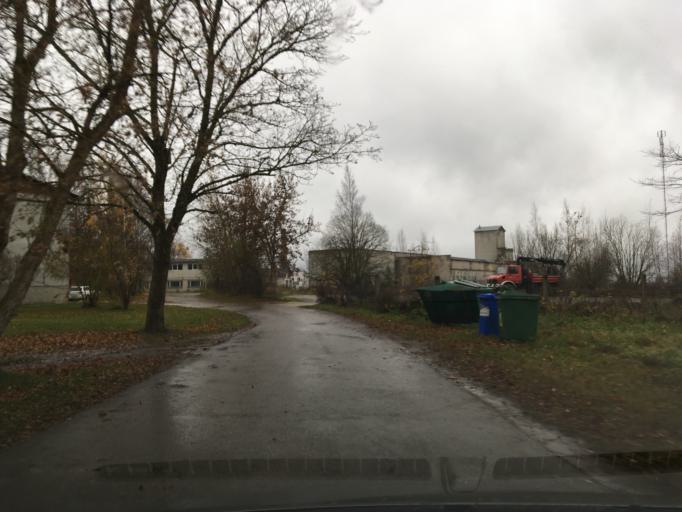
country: EE
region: Laeaene
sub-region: Lihula vald
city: Lihula
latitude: 58.6783
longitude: 23.8236
